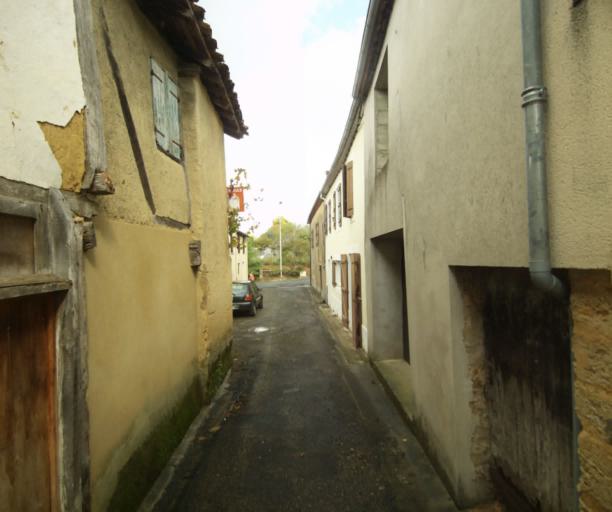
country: FR
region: Midi-Pyrenees
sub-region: Departement du Gers
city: Nogaro
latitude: 43.8208
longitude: -0.0891
